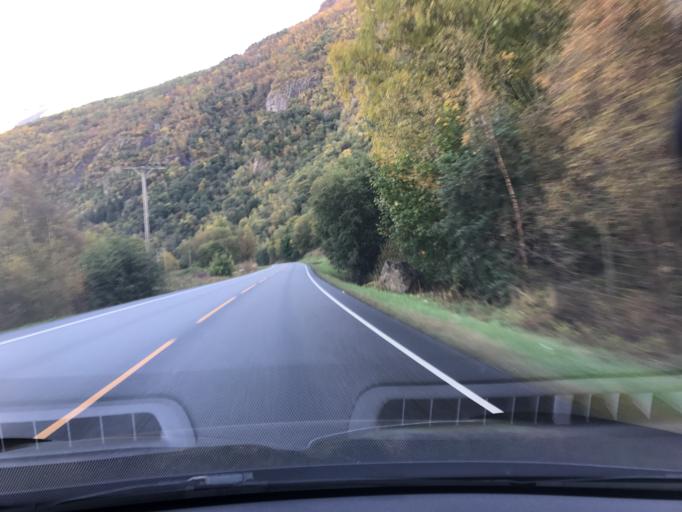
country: NO
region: Sogn og Fjordane
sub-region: Laerdal
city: Laerdalsoyri
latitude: 61.0970
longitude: 7.4767
